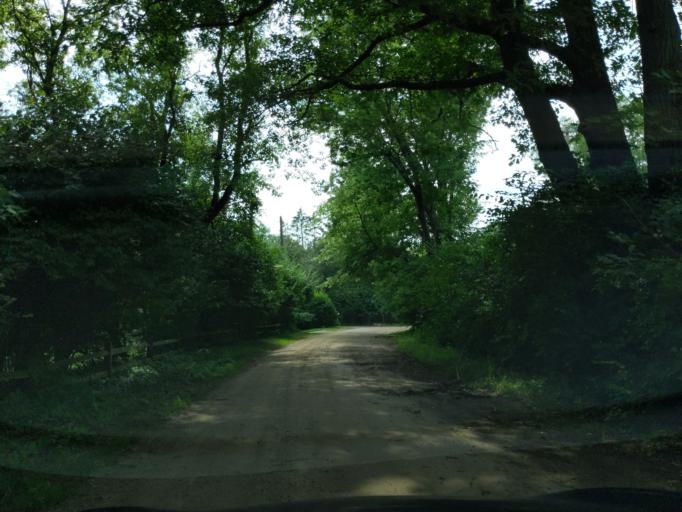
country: US
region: Michigan
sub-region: Ingham County
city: Okemos
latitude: 42.7239
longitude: -84.4426
